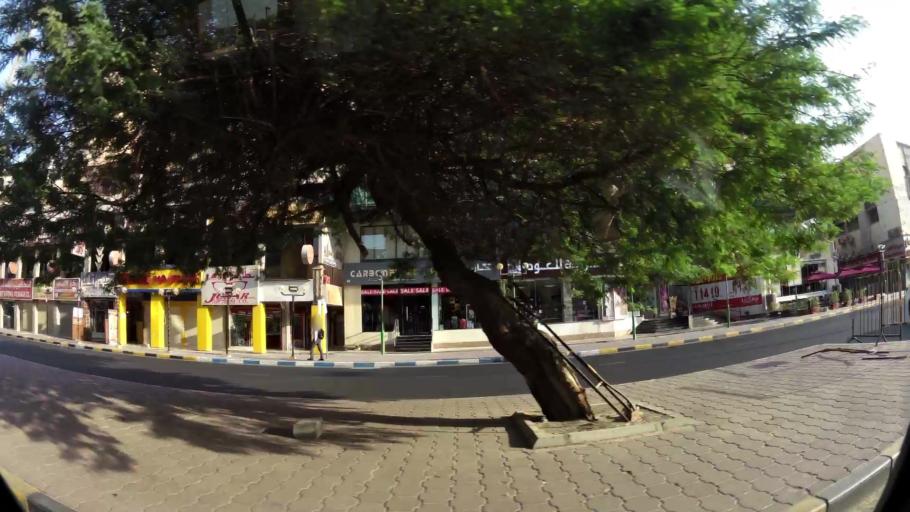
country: KW
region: Muhafazat Hawalli
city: As Salimiyah
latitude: 29.3389
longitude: 48.0683
